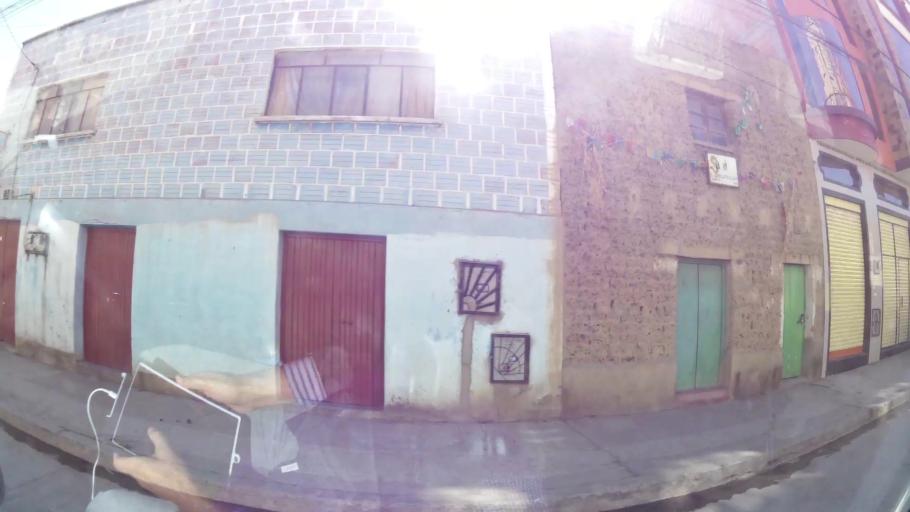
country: BO
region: La Paz
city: La Paz
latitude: -16.4961
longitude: -68.1766
